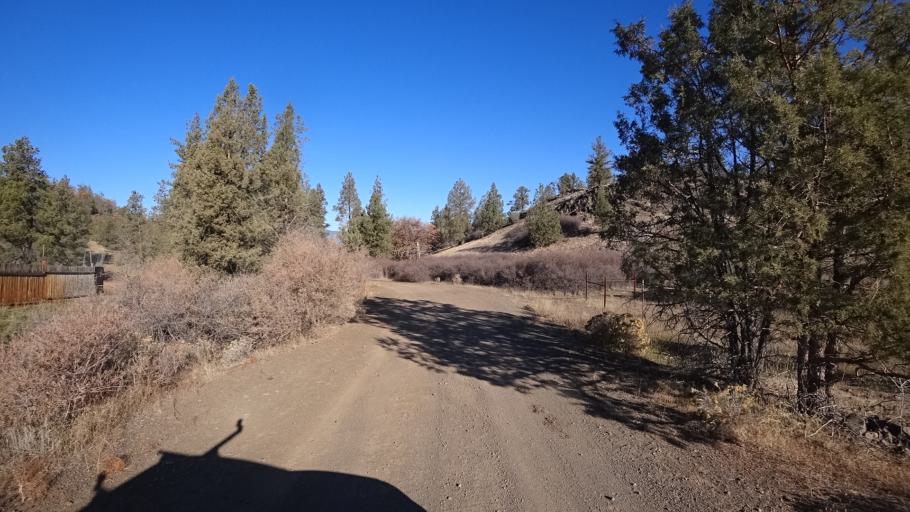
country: US
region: California
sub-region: Siskiyou County
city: Montague
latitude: 41.9175
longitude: -122.4228
